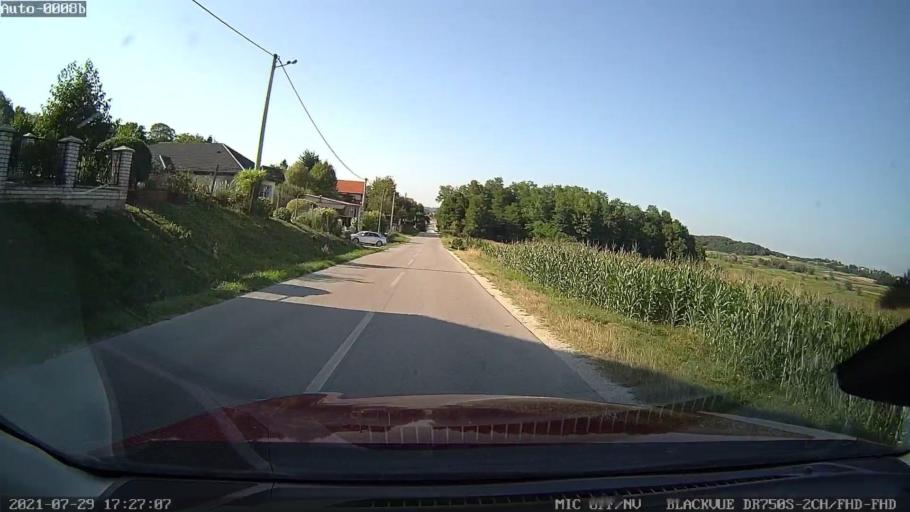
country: HR
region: Varazdinska
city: Ivanec
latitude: 46.2590
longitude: 16.1170
